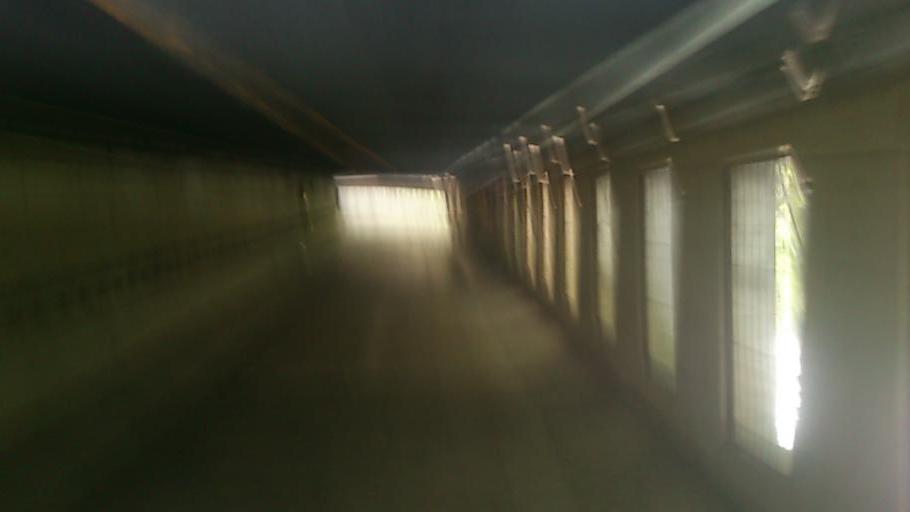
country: JP
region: Hokkaido
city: Bihoro
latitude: 43.4575
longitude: 144.2413
